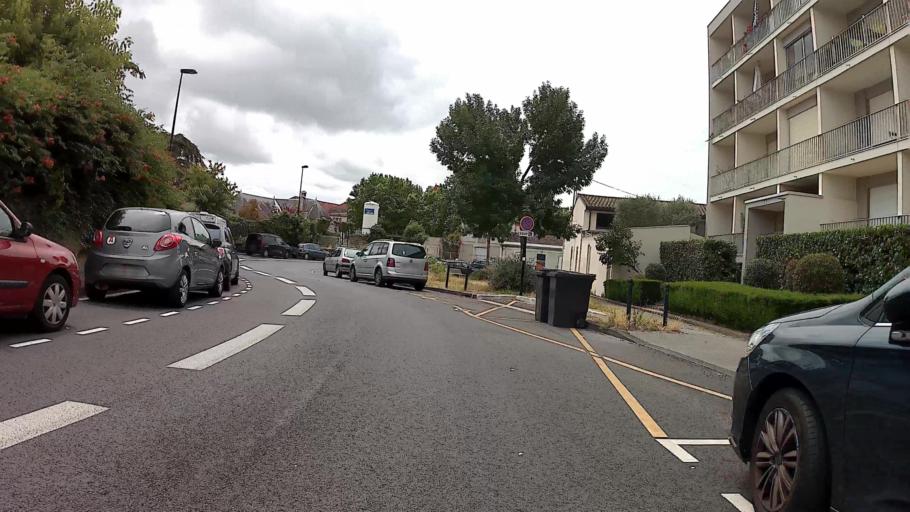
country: FR
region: Aquitaine
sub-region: Departement de la Gironde
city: Merignac
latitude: 44.8272
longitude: -0.6112
